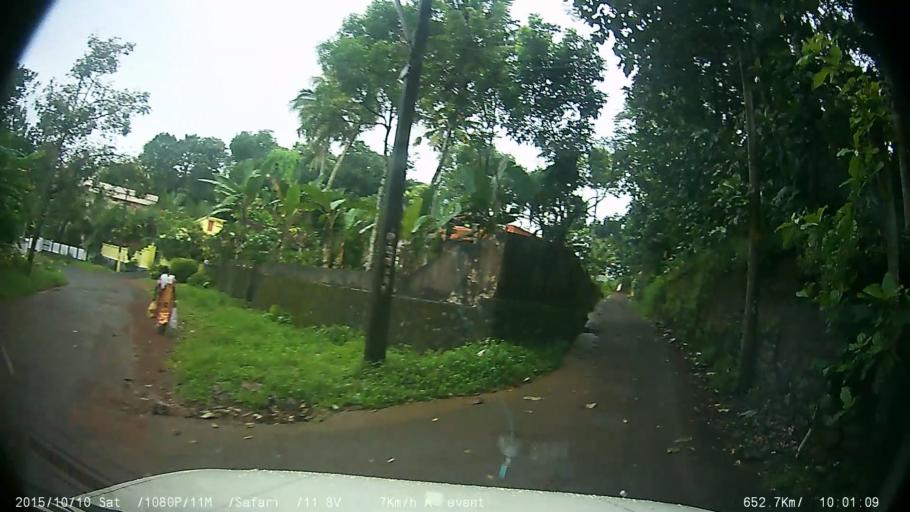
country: IN
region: Kerala
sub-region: Kottayam
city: Kottayam
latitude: 9.6389
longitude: 76.5368
